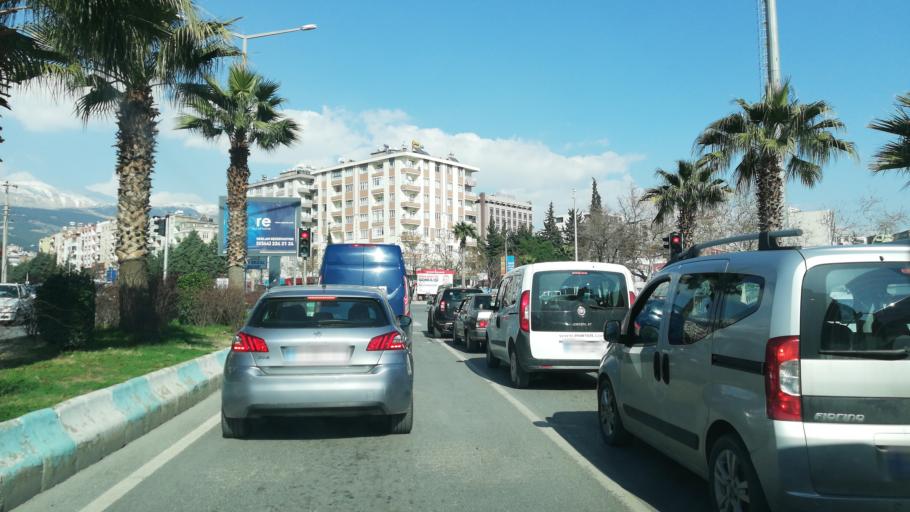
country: TR
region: Kahramanmaras
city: Kahramanmaras
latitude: 37.5749
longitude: 36.9223
